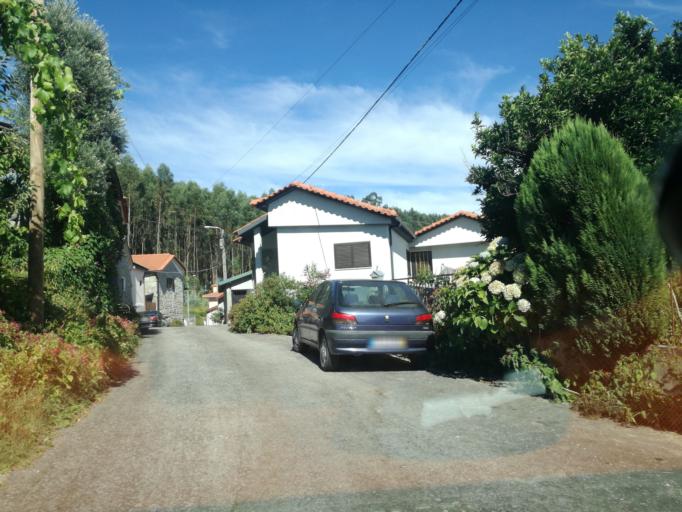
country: PT
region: Braga
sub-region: Fafe
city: Aroes
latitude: 41.4940
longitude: -8.2301
